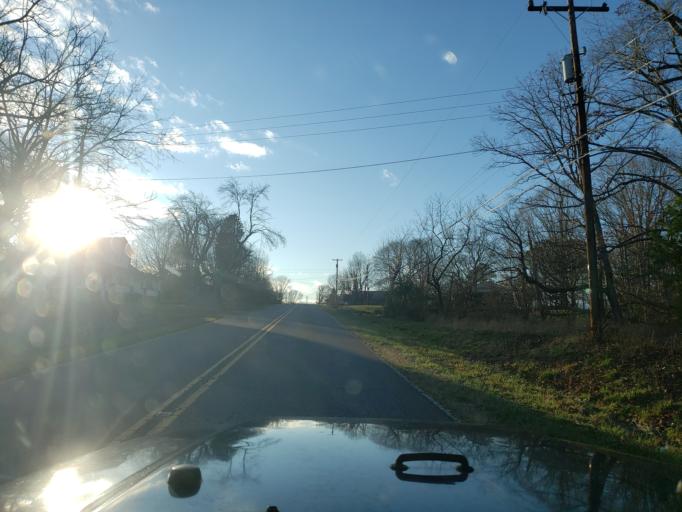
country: US
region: North Carolina
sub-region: Cleveland County
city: Shelby
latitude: 35.4150
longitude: -81.5822
